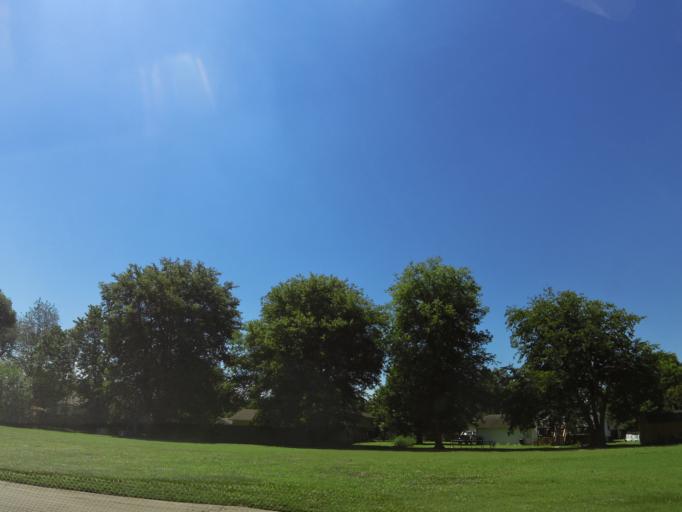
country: US
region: Missouri
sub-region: New Madrid County
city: New Madrid
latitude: 36.5995
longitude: -89.5285
